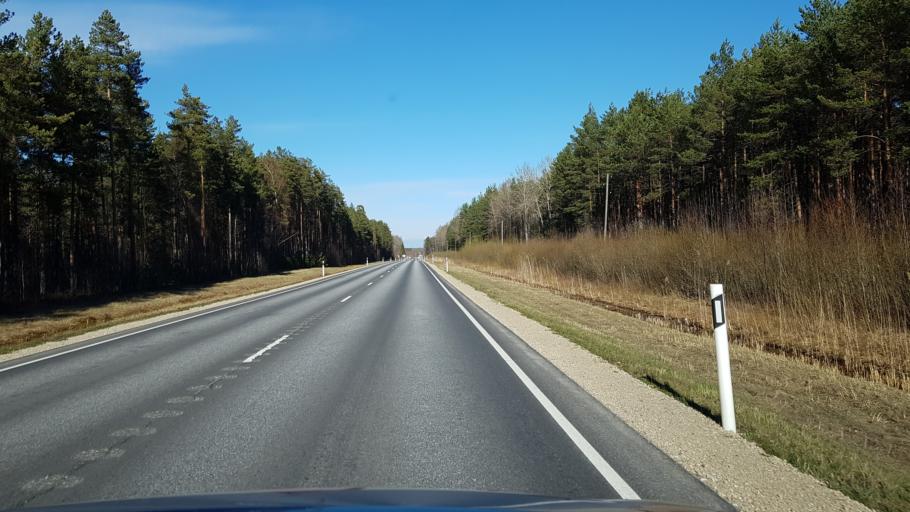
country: EE
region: Jogevamaa
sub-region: Mustvee linn
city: Mustvee
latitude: 58.9807
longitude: 27.1559
